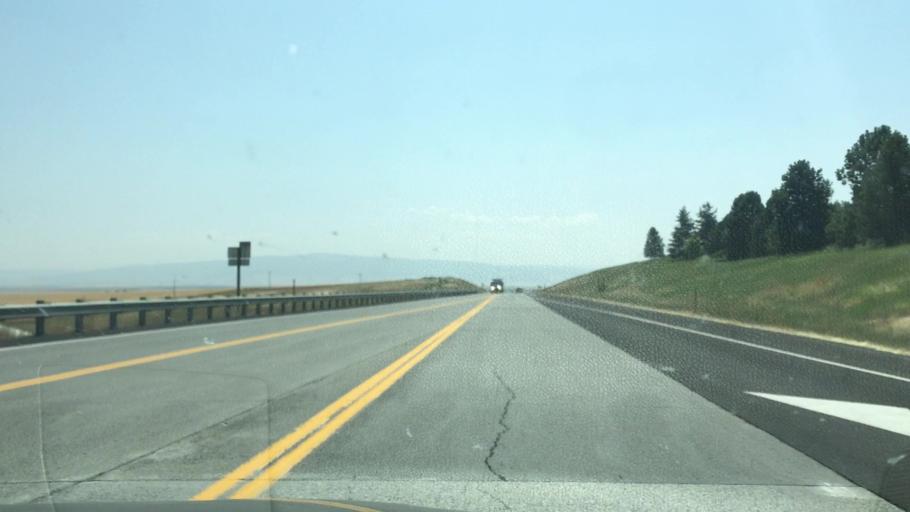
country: US
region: Idaho
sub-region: Lewis County
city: Nezperce
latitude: 46.0436
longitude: -116.3424
